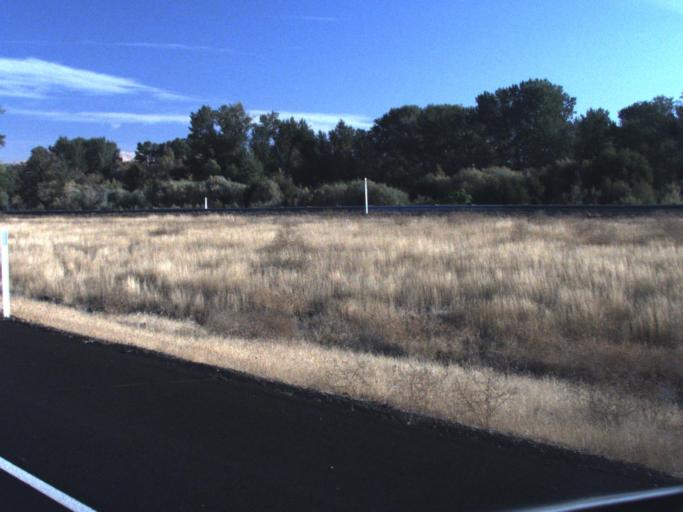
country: US
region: Washington
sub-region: Yakima County
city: Union Gap
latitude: 46.5445
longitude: -120.4705
